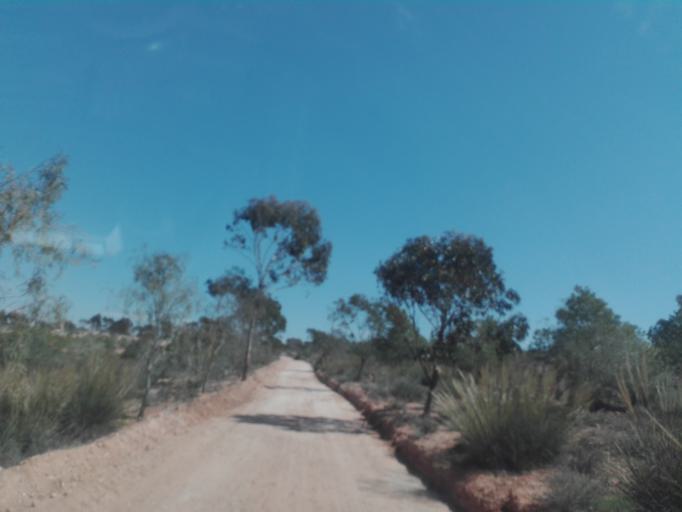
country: TN
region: Safaqis
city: Sfax
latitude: 34.6985
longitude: 10.5304
